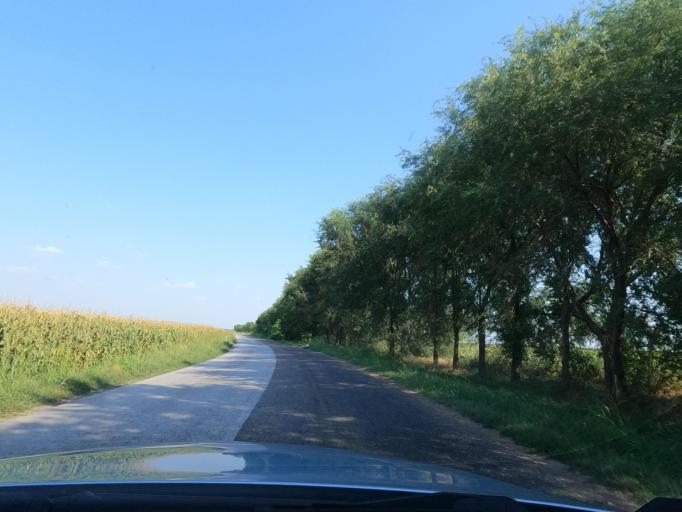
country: RS
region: Autonomna Pokrajina Vojvodina
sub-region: Juznobacki Okrug
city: Becej
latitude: 45.6531
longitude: 19.9670
